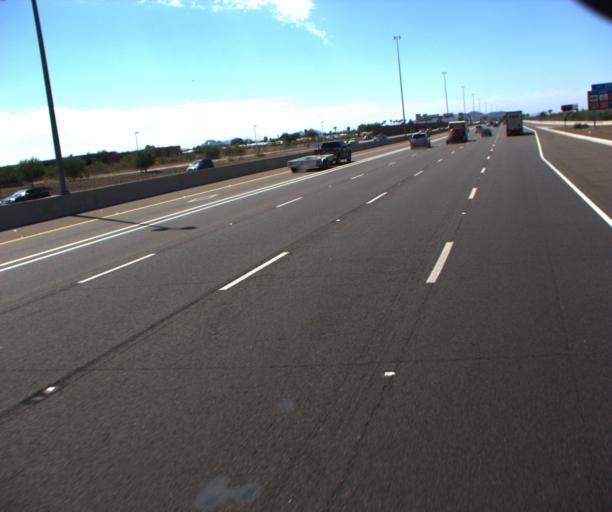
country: US
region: Arizona
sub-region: Maricopa County
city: Peoria
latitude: 33.6986
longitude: -112.1147
